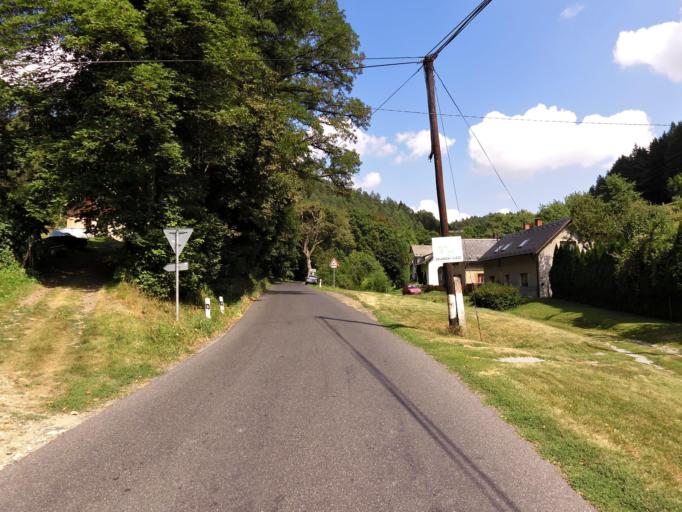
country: CZ
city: Cesky Dub
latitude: 50.6112
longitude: 14.9825
